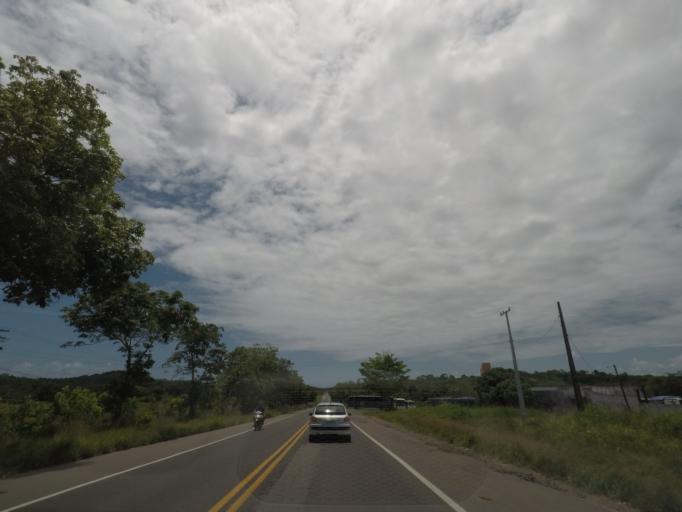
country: BR
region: Bahia
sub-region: Itaparica
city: Itaparica
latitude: -12.9431
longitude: -38.6318
